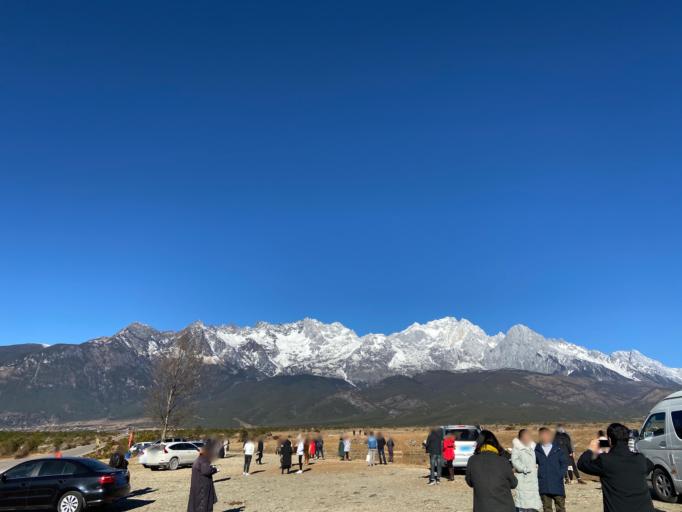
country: CN
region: Yunnan
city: Lijiang
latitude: 27.0113
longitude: 100.2561
